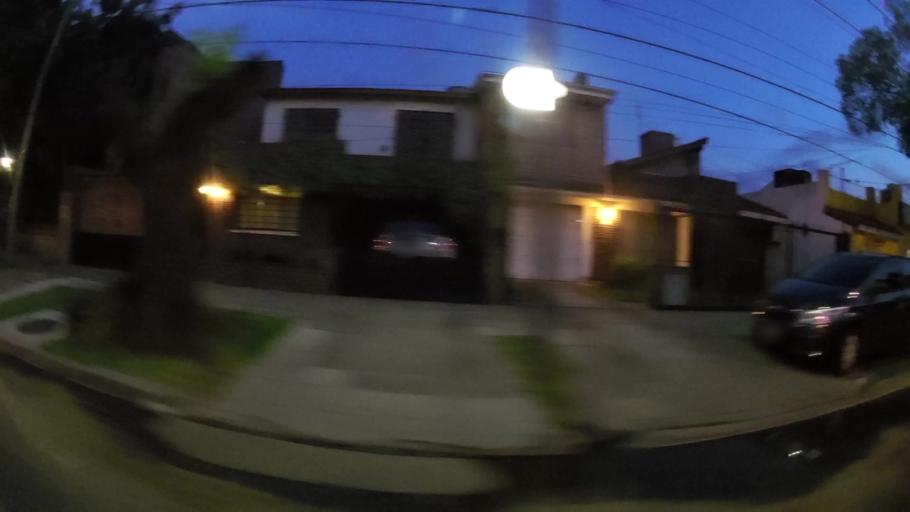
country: AR
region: Buenos Aires
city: Ituzaingo
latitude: -34.6528
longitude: -58.6590
